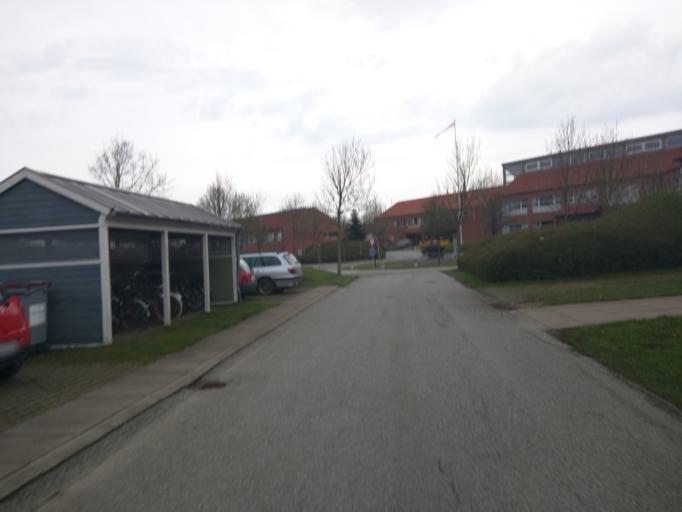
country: DK
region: Central Jutland
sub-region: Viborg Kommune
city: Bjerringbro
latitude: 56.4876
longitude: 9.5826
